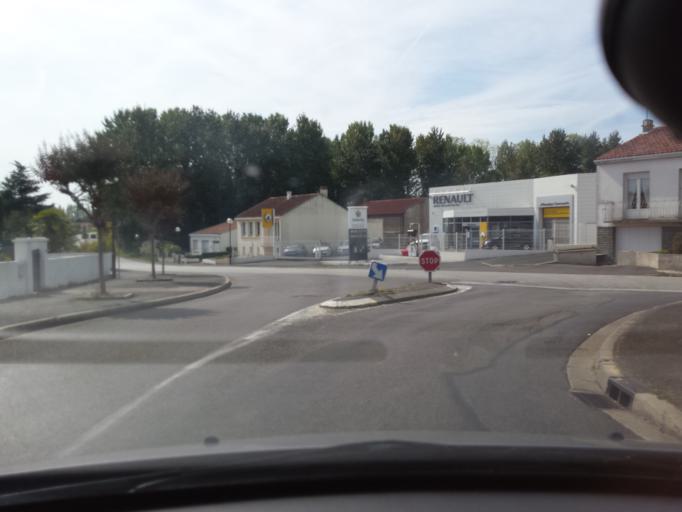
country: FR
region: Pays de la Loire
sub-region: Departement de la Vendee
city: Nieul-le-Dolent
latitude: 46.5731
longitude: -1.5095
